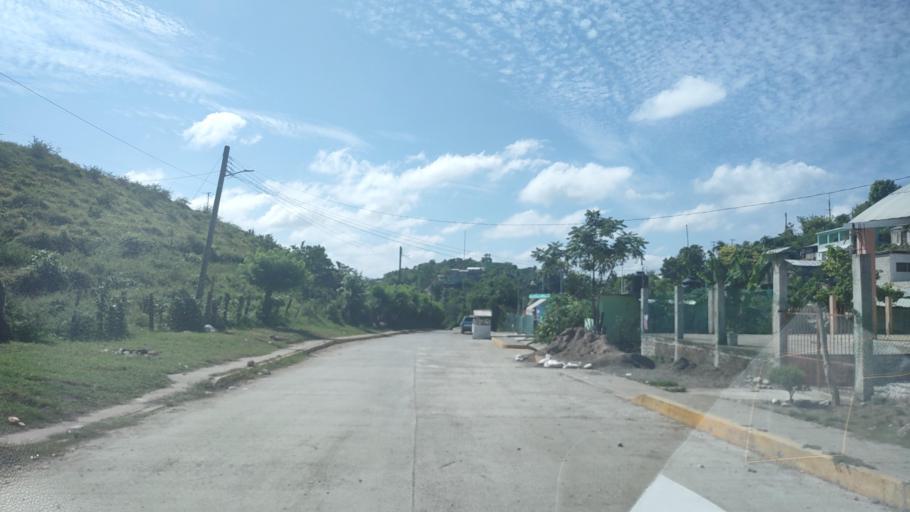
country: MM
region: Shan
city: Taunggyi
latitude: 20.5868
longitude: 97.3733
